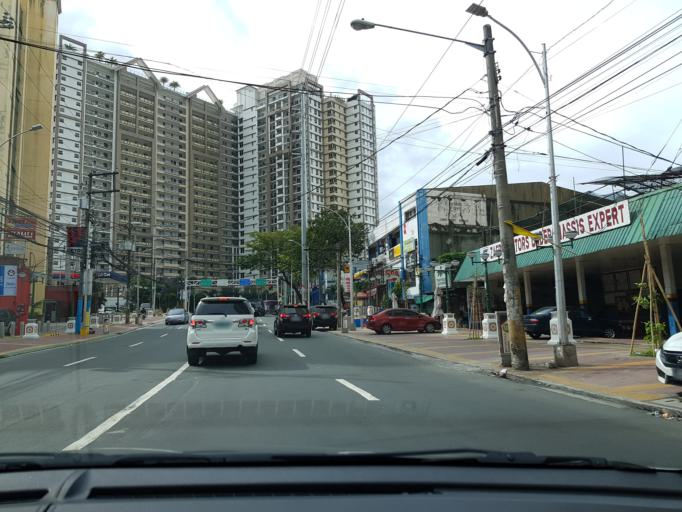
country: PH
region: Calabarzon
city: Del Monte
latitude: 14.6253
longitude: 121.0331
